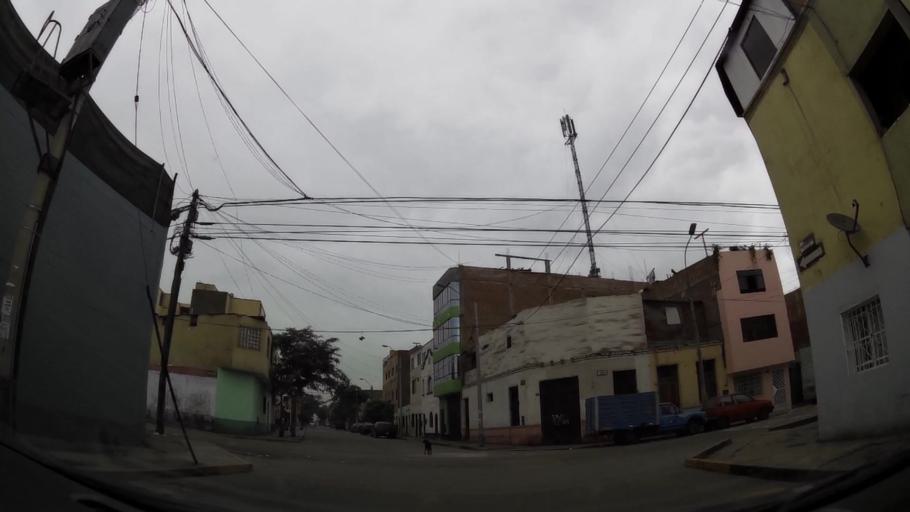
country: PE
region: Lima
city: Lima
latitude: -12.0521
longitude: -77.0532
